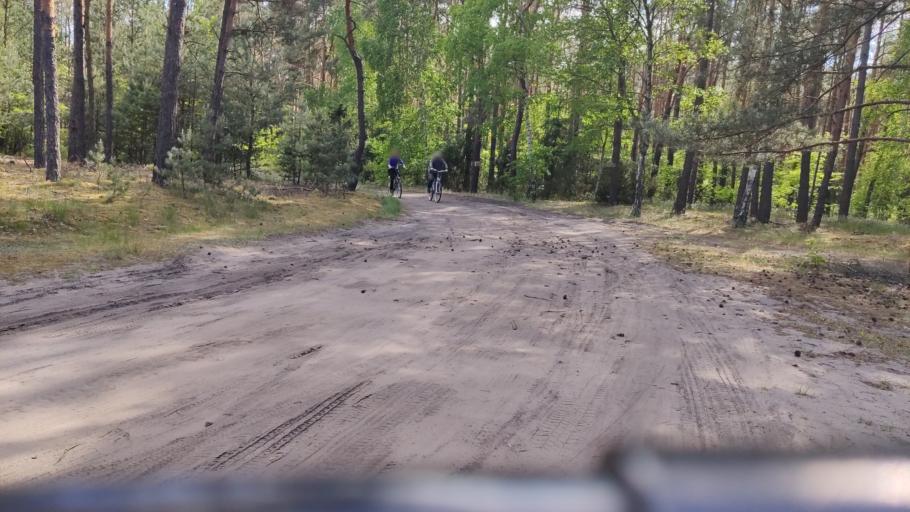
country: PL
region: Kujawsko-Pomorskie
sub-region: Wloclawek
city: Wloclawek
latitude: 52.6048
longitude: 19.0736
